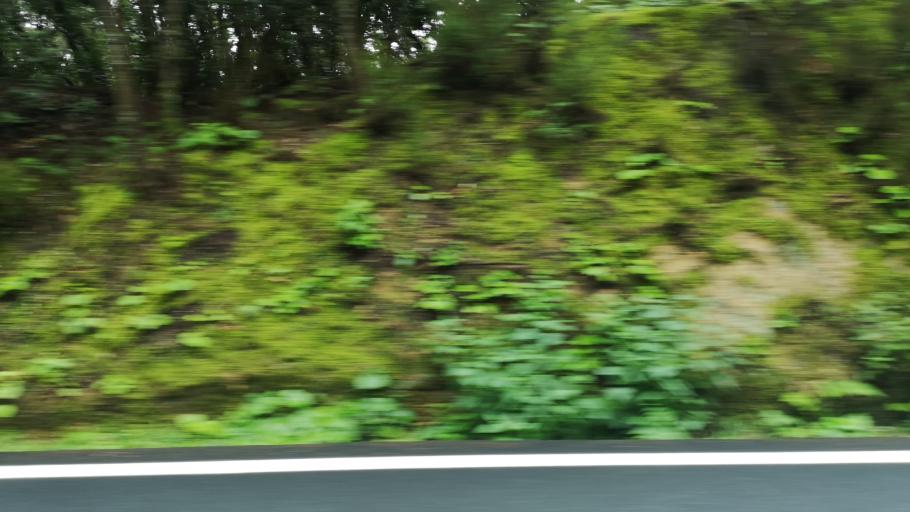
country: ES
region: Canary Islands
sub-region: Provincia de Santa Cruz de Tenerife
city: Vallehermosa
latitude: 28.1269
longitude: -17.2594
